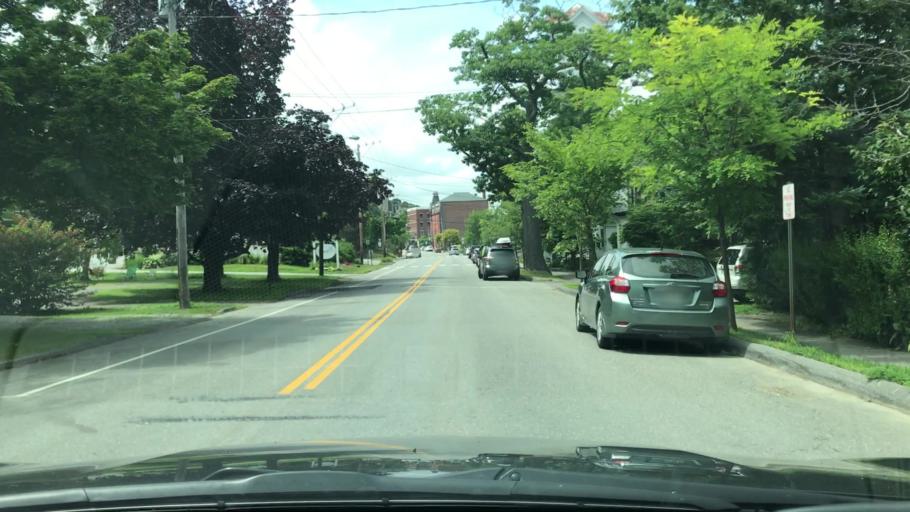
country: US
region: Maine
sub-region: Waldo County
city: Belfast
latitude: 44.4245
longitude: -69.0034
